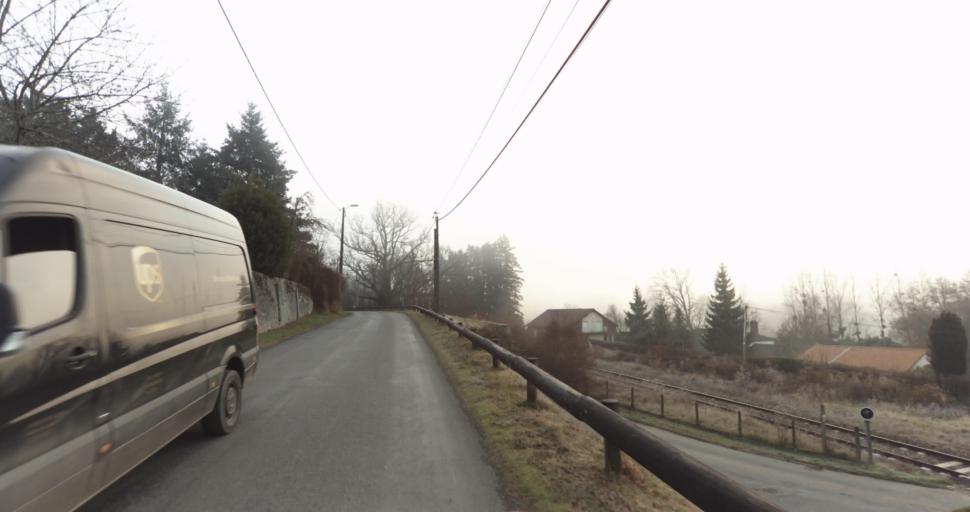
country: FR
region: Limousin
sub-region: Departement de la Haute-Vienne
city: Aixe-sur-Vienne
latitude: 45.8010
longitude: 1.1285
